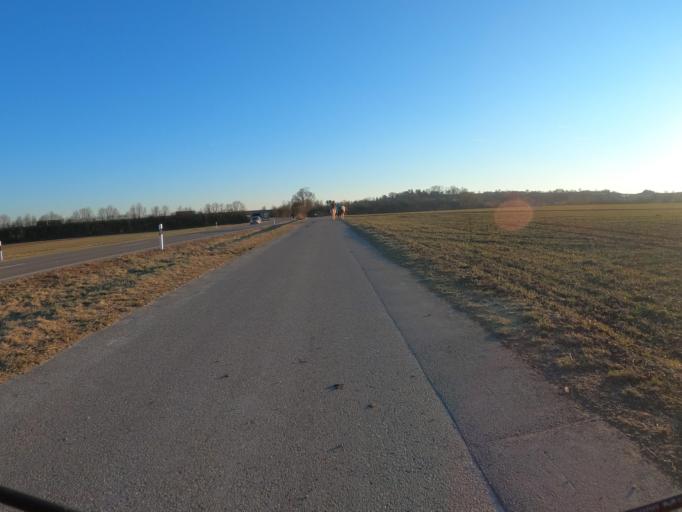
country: DE
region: Baden-Wuerttemberg
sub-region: Tuebingen Region
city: Langenau
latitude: 48.4687
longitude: 10.1069
